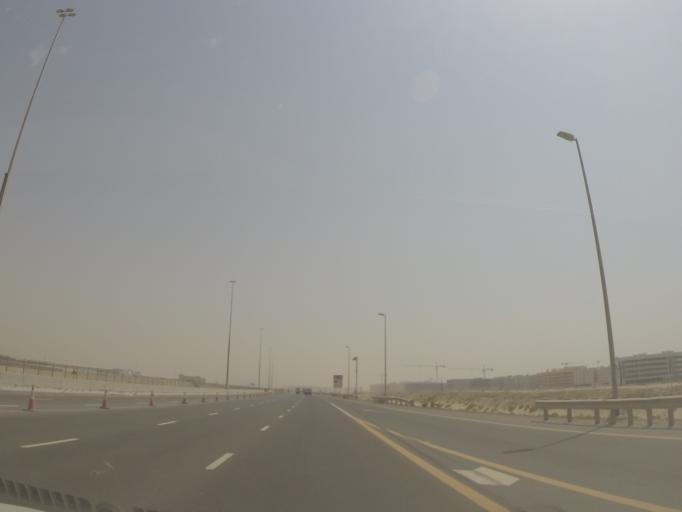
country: AE
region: Dubai
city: Dubai
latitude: 25.0015
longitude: 55.1487
